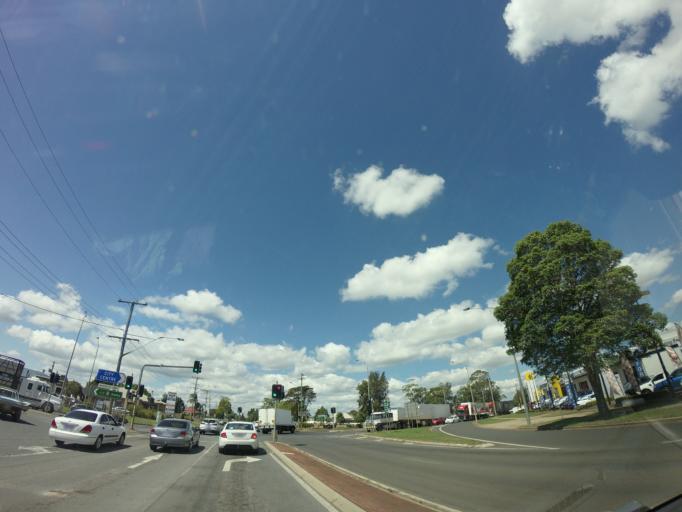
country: AU
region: Queensland
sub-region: Toowoomba
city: Toowoomba
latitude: -27.5661
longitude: 151.9295
